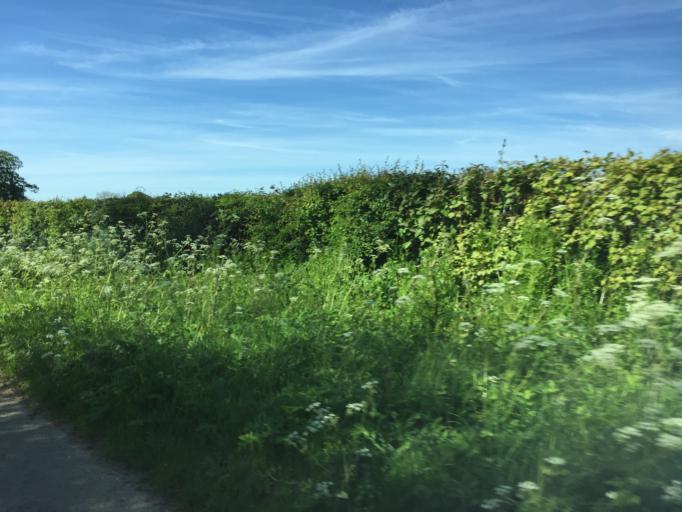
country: GB
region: England
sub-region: Wiltshire
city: Luckington
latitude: 51.5970
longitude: -2.2558
